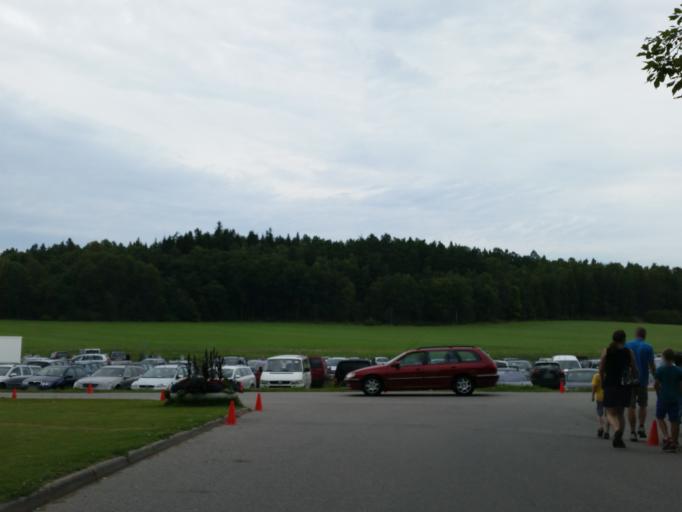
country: SE
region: Stockholm
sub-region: Botkyrka Kommun
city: Tumba
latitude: 59.2218
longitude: 17.8319
